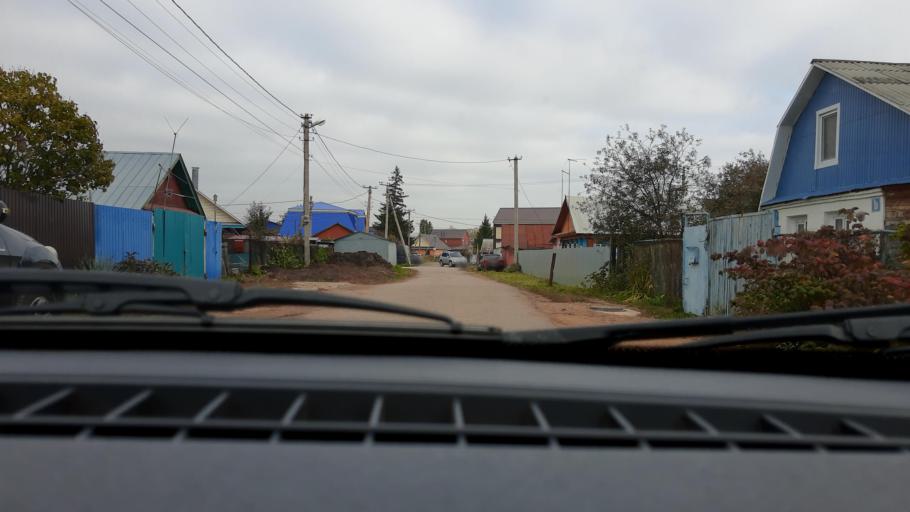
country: RU
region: Bashkortostan
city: Mikhaylovka
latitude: 54.7930
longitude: 55.8833
